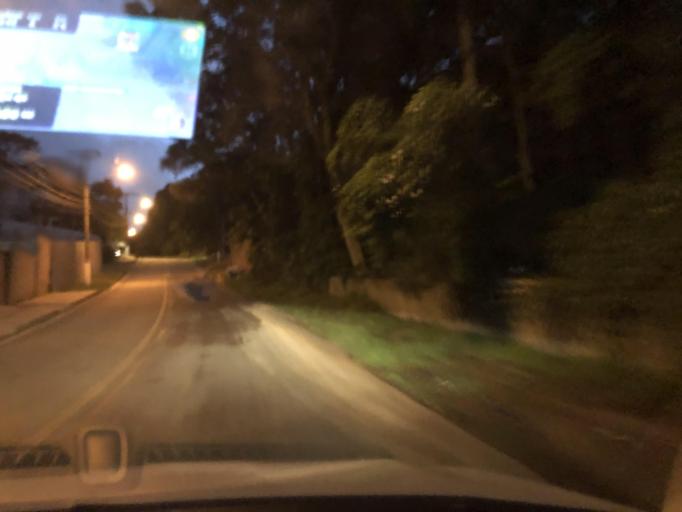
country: BR
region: Santa Catarina
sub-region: Florianopolis
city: Morro da Cruz
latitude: -27.5852
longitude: -48.5362
